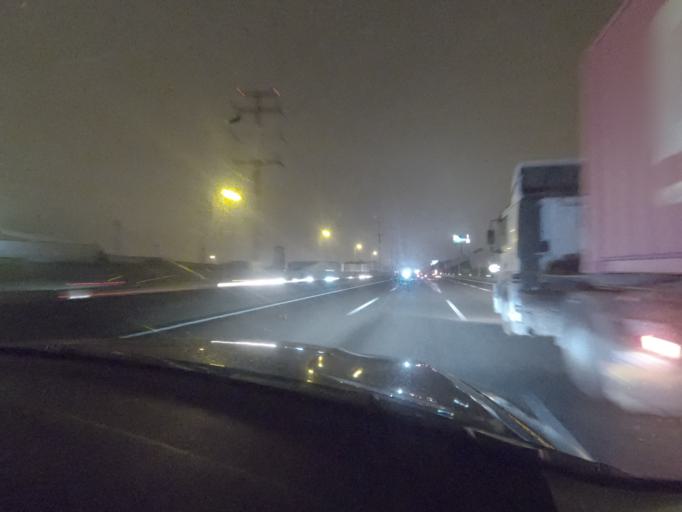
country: PT
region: Lisbon
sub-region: Loures
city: Santa Iria da Azoia
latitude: 38.8466
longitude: -9.0906
